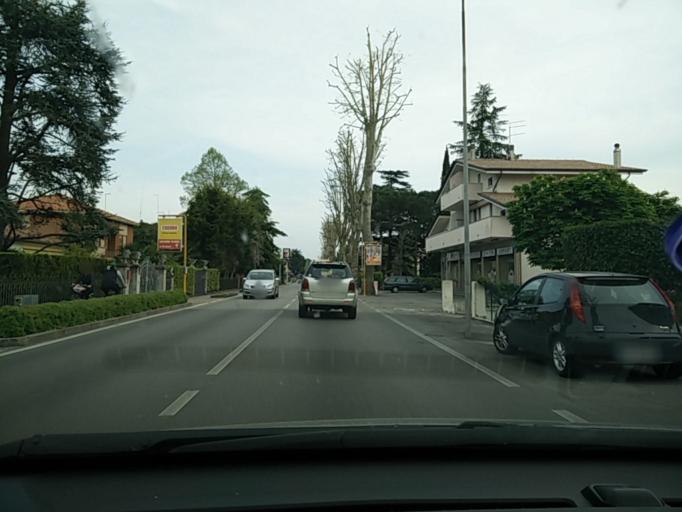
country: IT
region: Veneto
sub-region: Provincia di Venezia
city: San Dona di Piave
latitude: 45.6431
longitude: 12.5520
